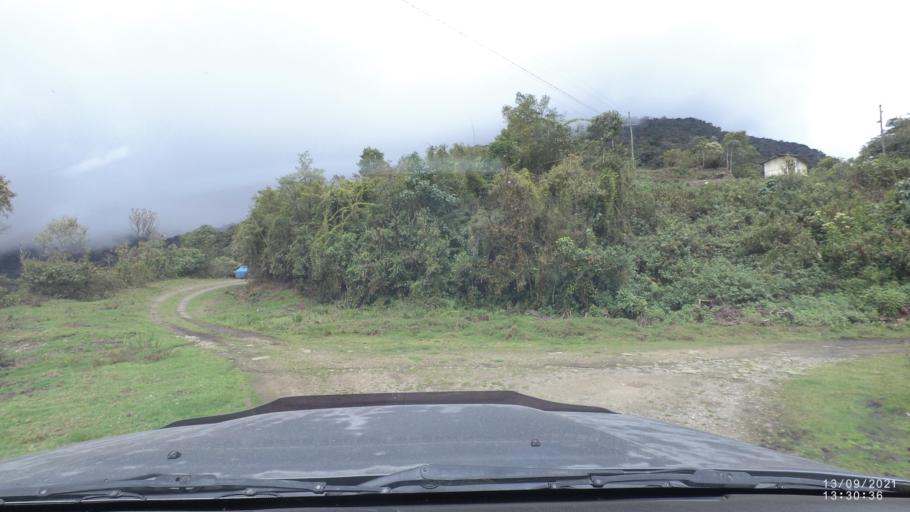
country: BO
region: Cochabamba
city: Colomi
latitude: -17.2188
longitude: -65.8610
